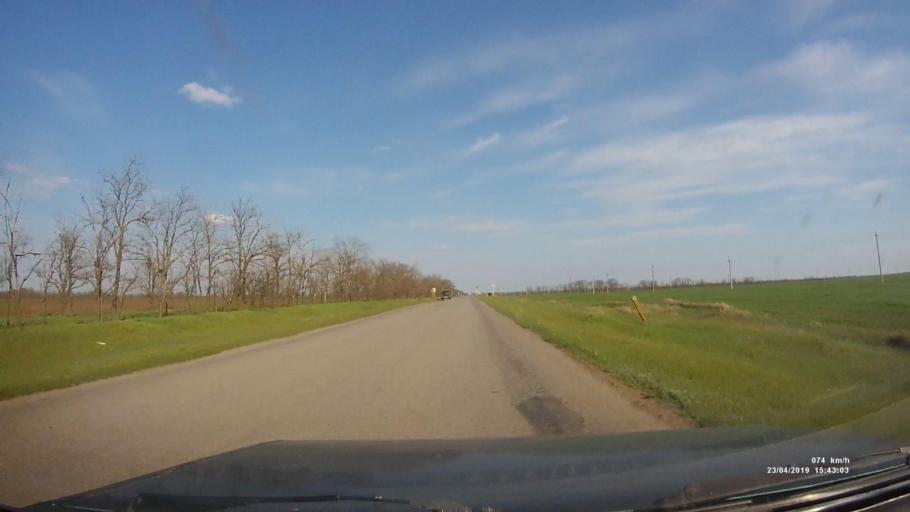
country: RU
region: Rostov
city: Remontnoye
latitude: 46.5461
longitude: 43.0765
